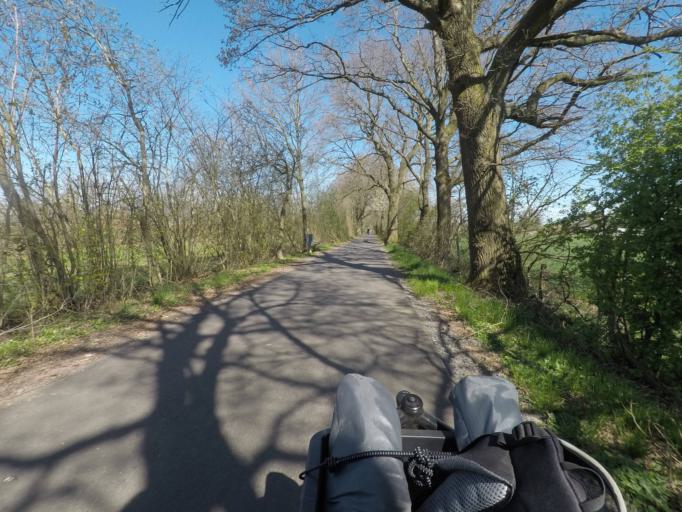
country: DE
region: Schleswig-Holstein
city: Braak
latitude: 53.6050
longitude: 10.2798
